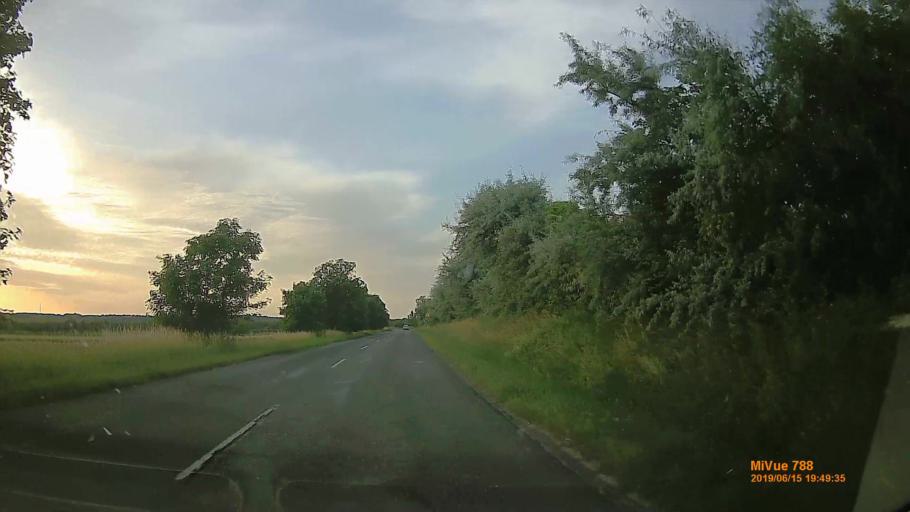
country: HU
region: Veszprem
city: Szentkiralyszabadja
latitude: 47.0365
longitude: 17.9318
